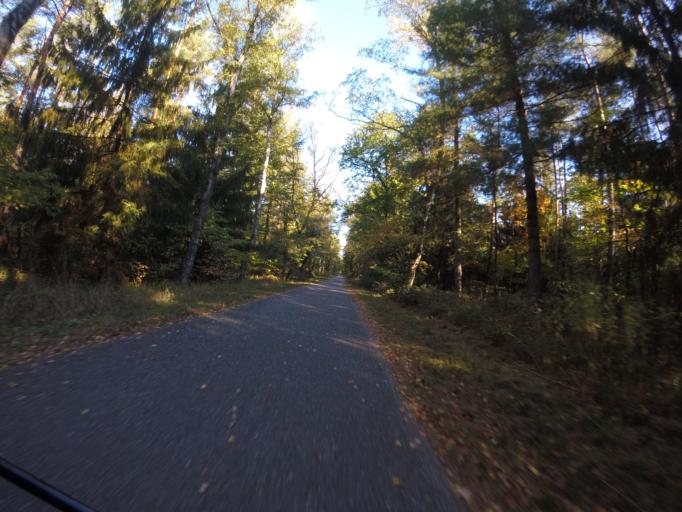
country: DE
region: Baden-Wuerttemberg
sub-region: Karlsruhe Region
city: Eggenstein-Leopoldshafen
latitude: 49.0513
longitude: 8.4084
